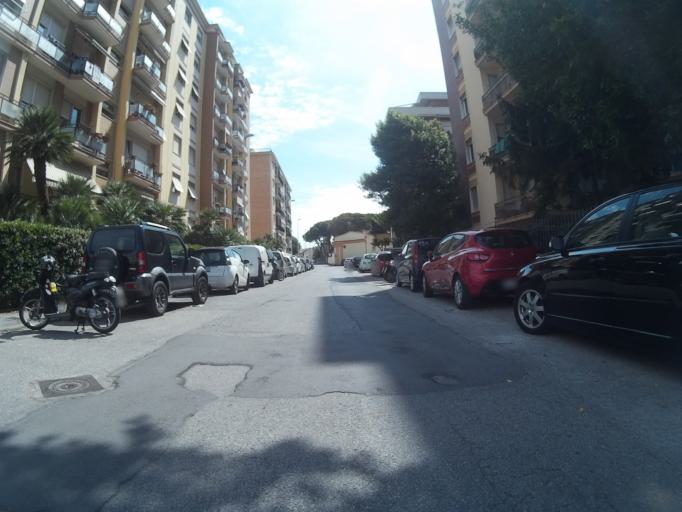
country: IT
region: Tuscany
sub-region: Provincia di Livorno
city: Livorno
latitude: 43.5462
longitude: 10.3245
